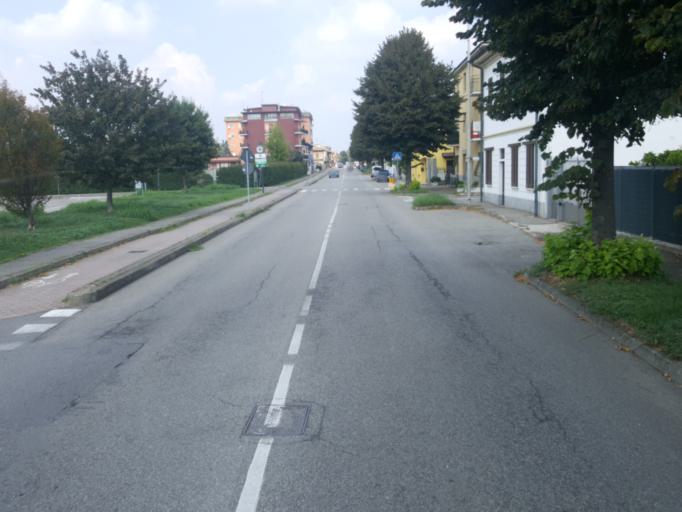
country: IT
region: Lombardy
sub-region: Citta metropolitana di Milano
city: Abbiategrasso
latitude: 45.3854
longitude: 8.9131
